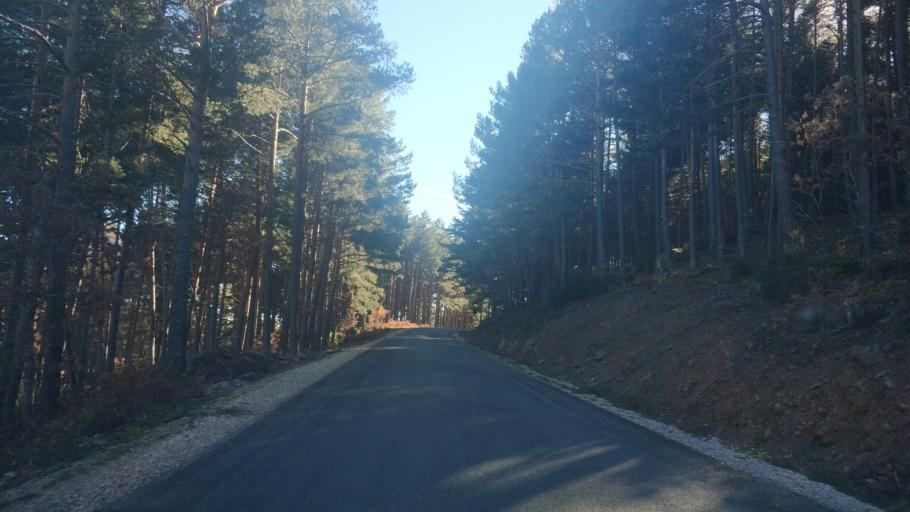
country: ES
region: Castille and Leon
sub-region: Provincia de Soria
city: Vinuesa
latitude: 41.9750
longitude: -2.7946
